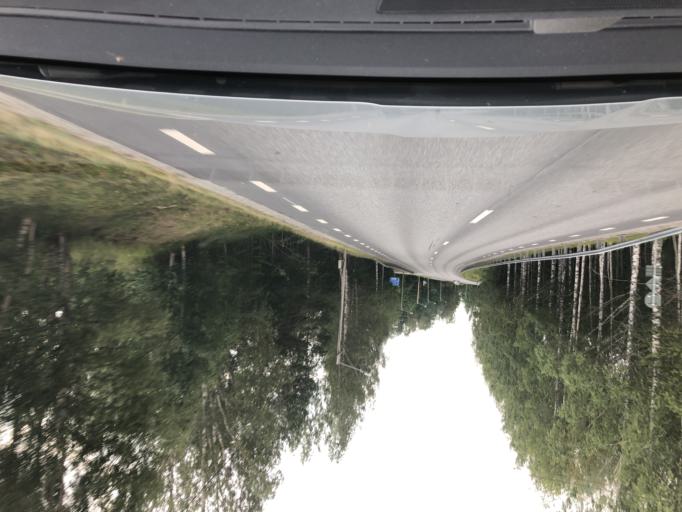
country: SE
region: Vaesternorrland
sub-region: Solleftea Kommun
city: Solleftea
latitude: 63.2427
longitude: 17.2071
